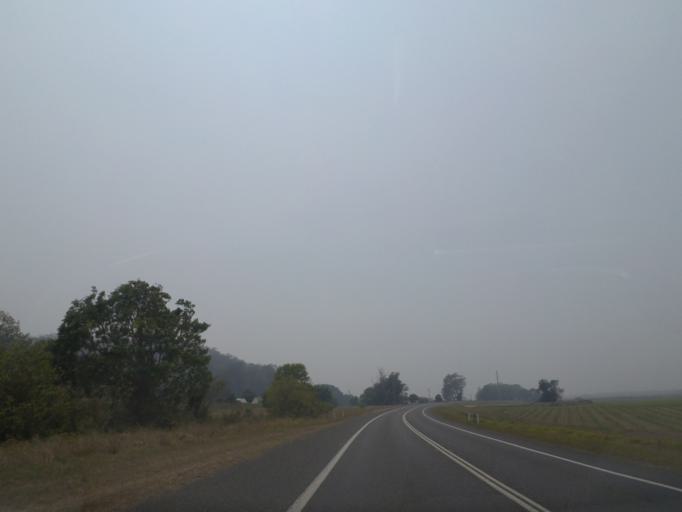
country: AU
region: New South Wales
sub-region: Clarence Valley
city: Maclean
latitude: -29.5412
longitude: 153.1595
